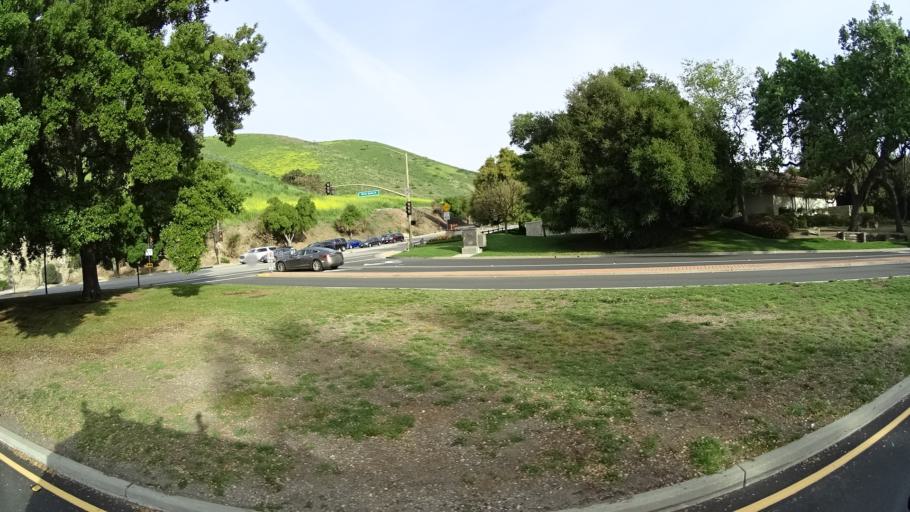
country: US
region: California
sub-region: Ventura County
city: Thousand Oaks
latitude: 34.1887
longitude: -118.8215
